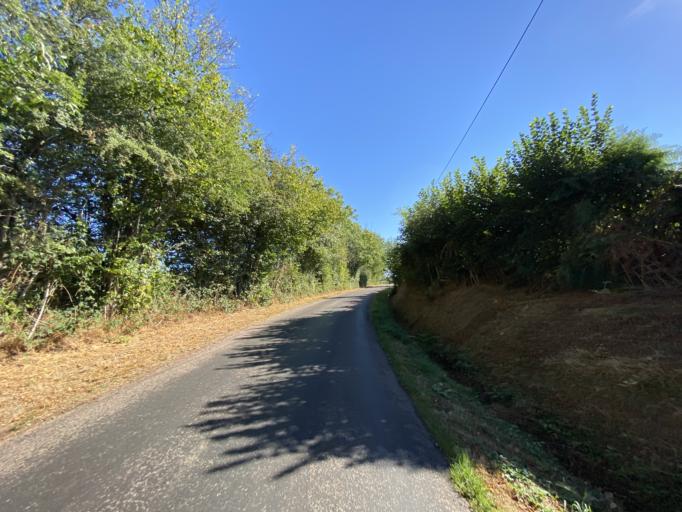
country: FR
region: Bourgogne
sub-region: Departement de la Cote-d'Or
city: Saulieu
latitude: 47.2761
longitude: 4.1829
